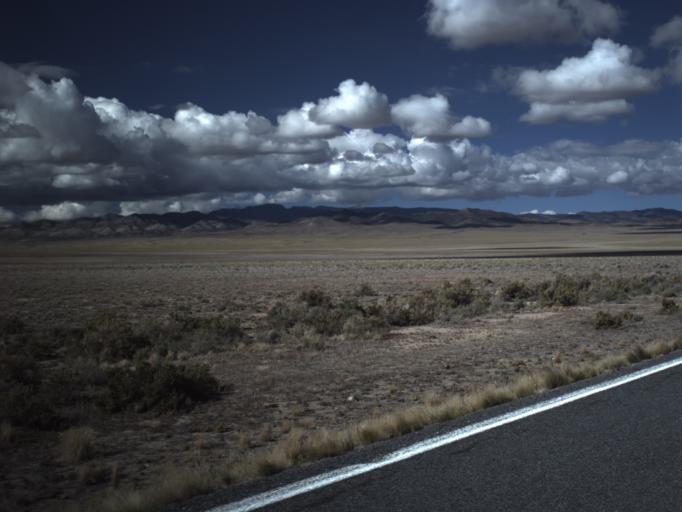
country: US
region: Utah
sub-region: Beaver County
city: Milford
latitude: 38.5454
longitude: -113.7173
